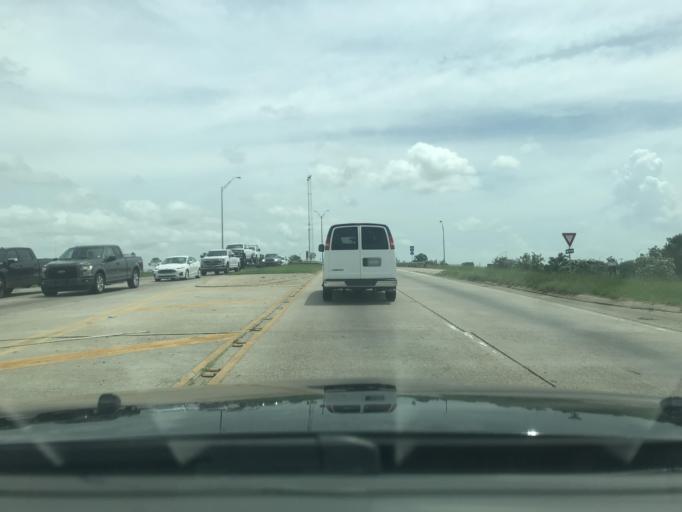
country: US
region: Louisiana
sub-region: Calcasieu Parish
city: Lake Charles
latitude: 30.2480
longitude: -93.1805
